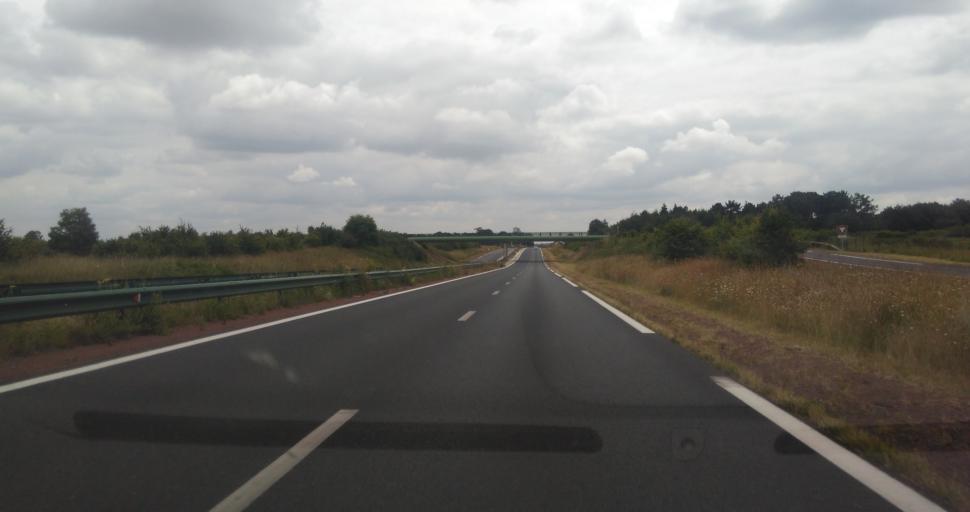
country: FR
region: Pays de la Loire
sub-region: Departement de la Vendee
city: Bournezeau
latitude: 46.6454
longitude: -1.2048
